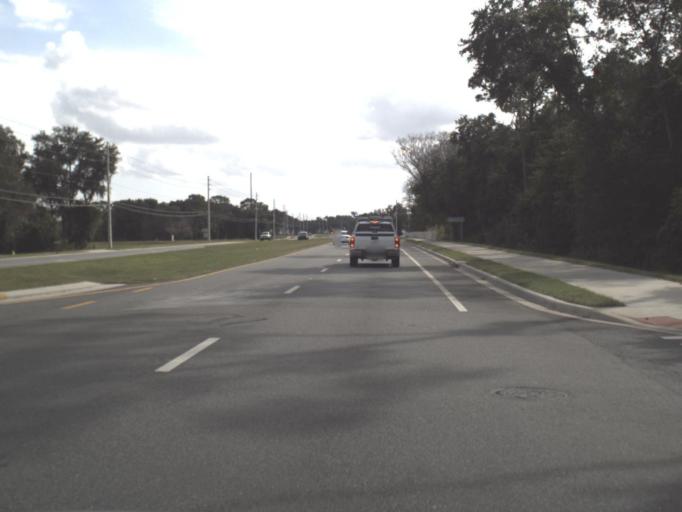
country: US
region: Florida
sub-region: Osceola County
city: Saint Cloud
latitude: 28.3048
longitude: -81.2394
